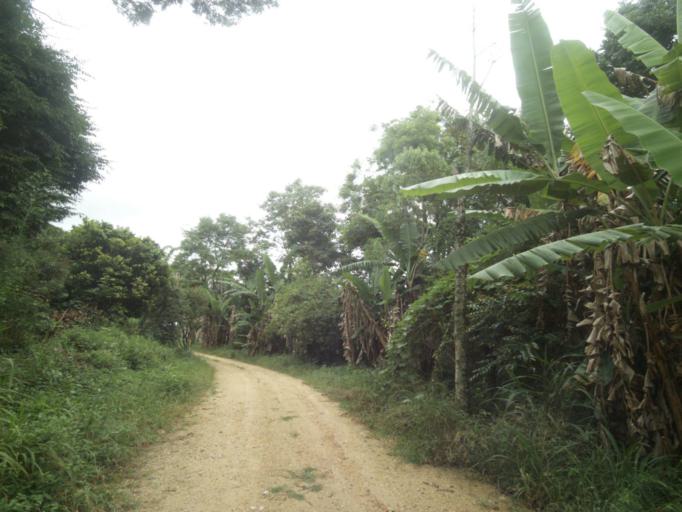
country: BR
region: Parana
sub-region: Curitiba
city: Curitiba
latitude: -25.4515
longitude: -49.3340
